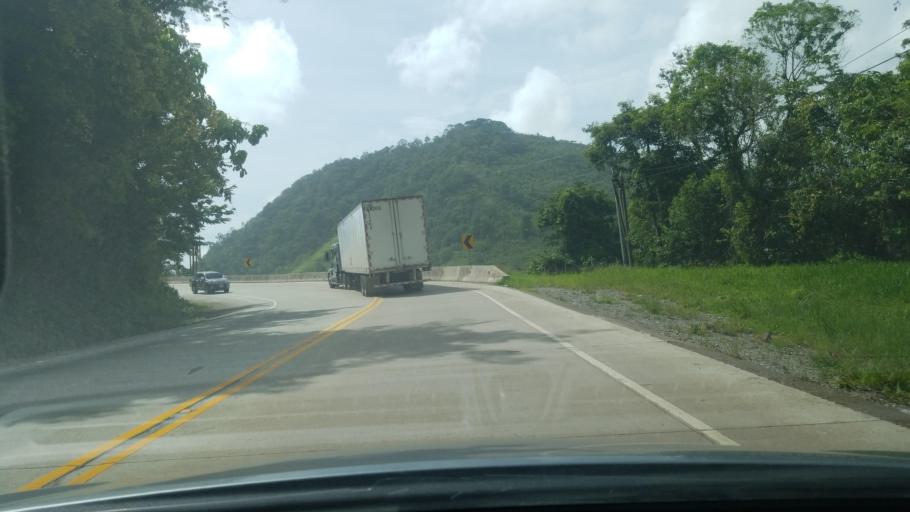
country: HN
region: Copan
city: San Jeronimo
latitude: 14.9310
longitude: -88.9564
